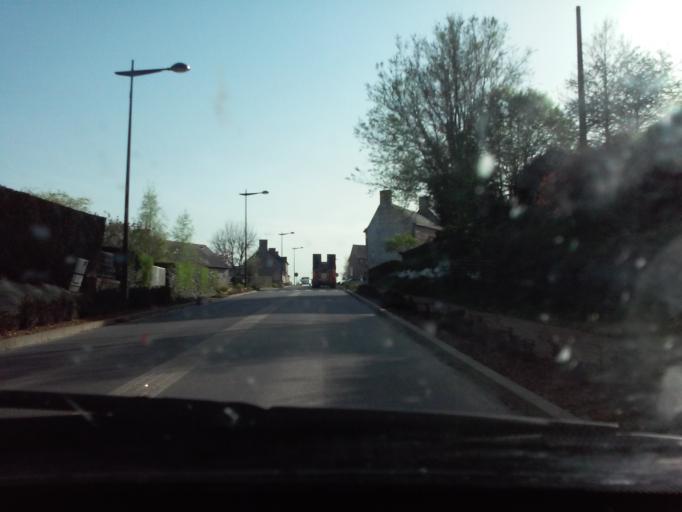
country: FR
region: Brittany
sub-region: Departement d'Ille-et-Vilaine
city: Saint-Jean-sur-Couesnon
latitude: 48.2911
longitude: -1.3685
